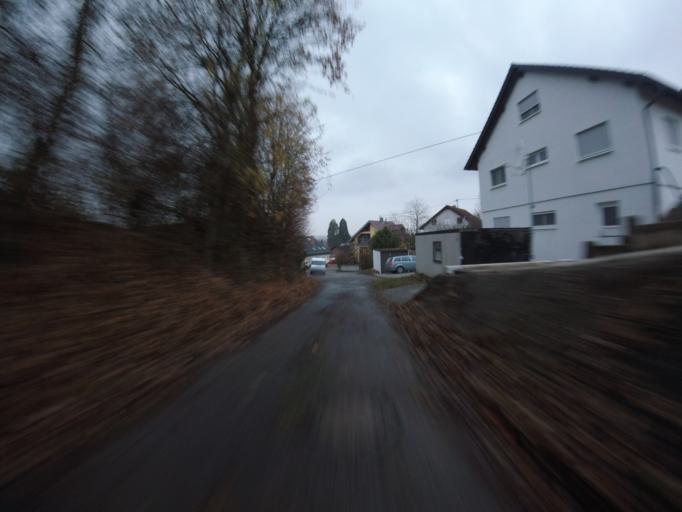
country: DE
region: Baden-Wuerttemberg
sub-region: Regierungsbezirk Stuttgart
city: Aspach
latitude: 48.9950
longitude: 9.3968
